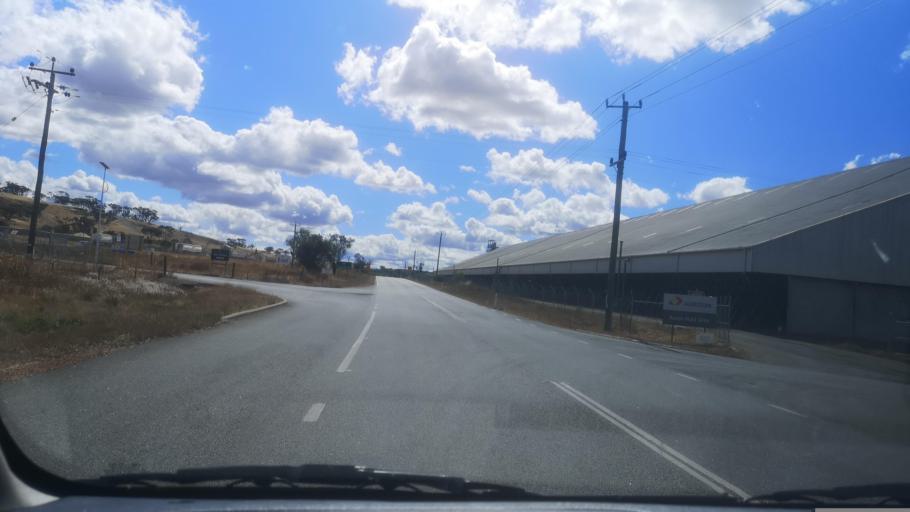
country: AU
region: Western Australia
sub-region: Northam
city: Northam
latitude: -31.6425
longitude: 116.6380
